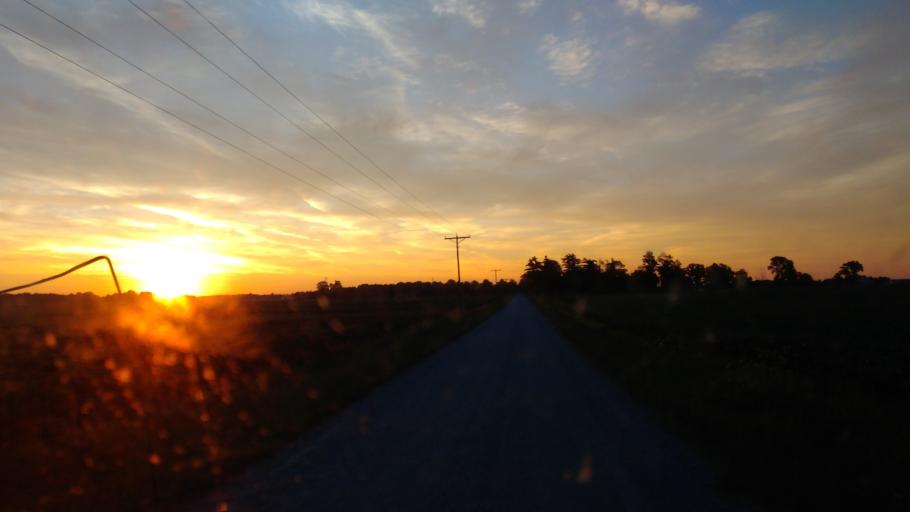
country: US
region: Indiana
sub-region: Wells County
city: Bluffton
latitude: 40.6845
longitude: -85.1137
